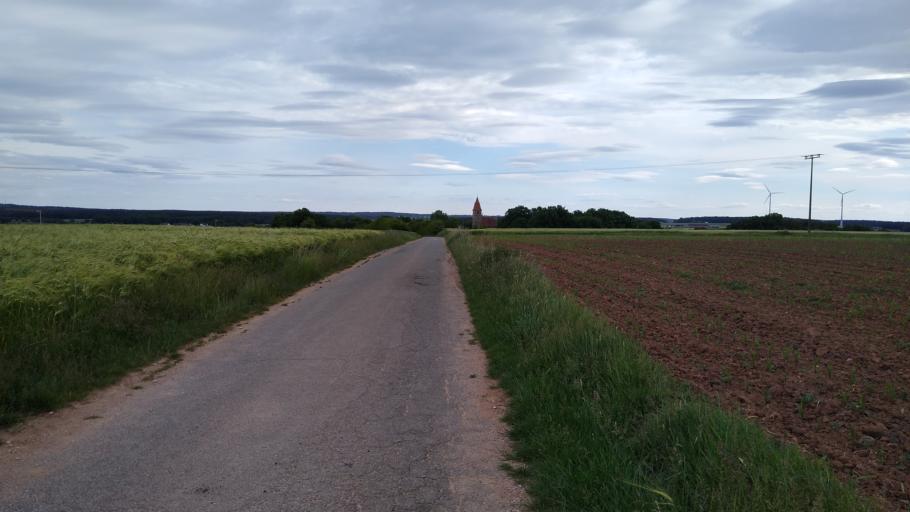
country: DE
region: Bavaria
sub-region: Regierungsbezirk Mittelfranken
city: Veitsbronn
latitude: 49.5185
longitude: 10.8885
